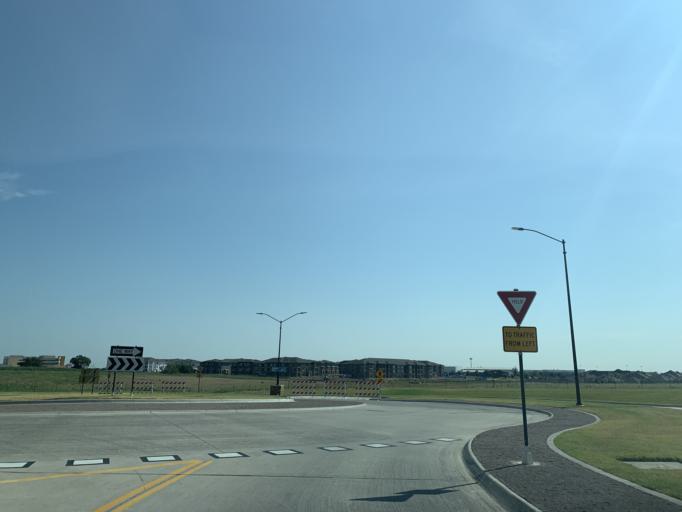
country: US
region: Texas
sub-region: Tarrant County
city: Keller
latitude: 32.9230
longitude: -97.3122
